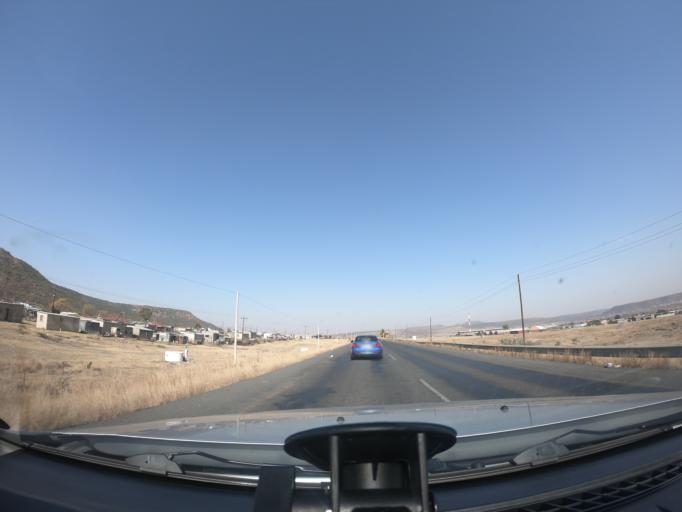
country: ZA
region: KwaZulu-Natal
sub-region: uThukela District Municipality
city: Ladysmith
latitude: -28.5683
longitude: 29.8350
